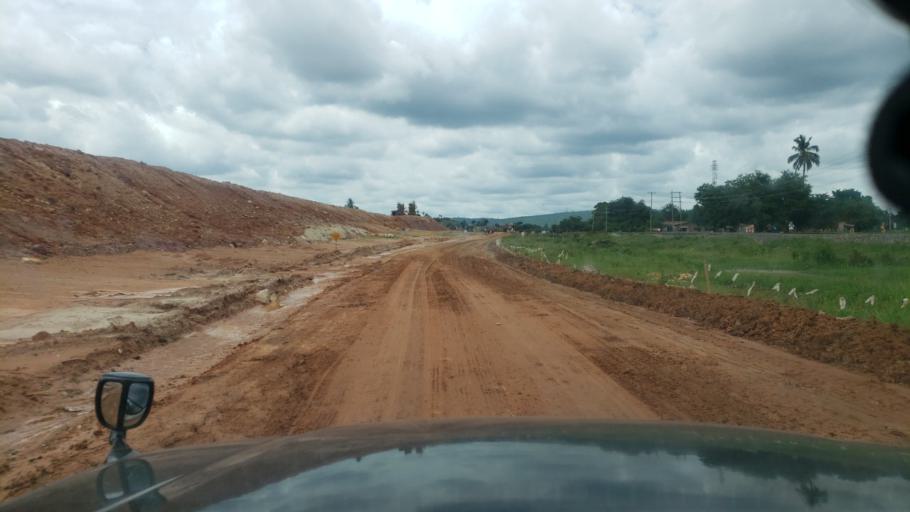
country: TZ
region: Pwani
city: Kisarawe
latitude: -6.8850
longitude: 39.1458
